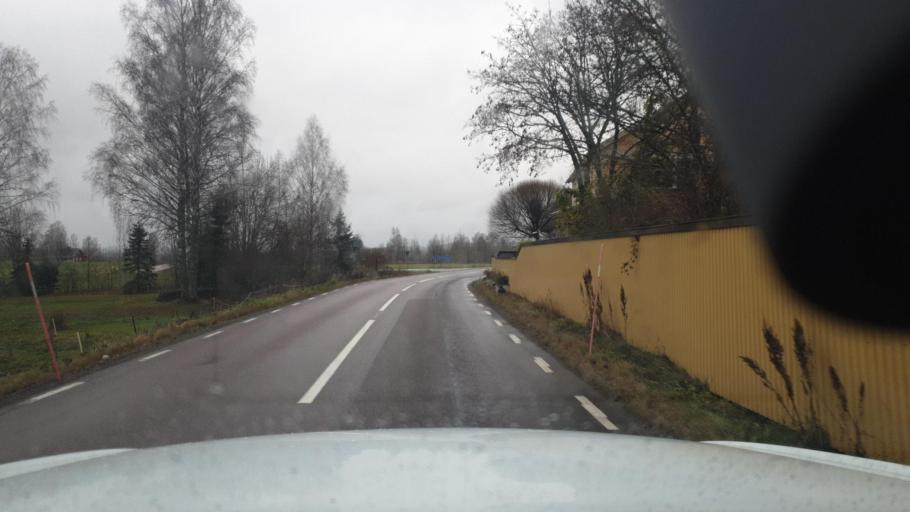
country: SE
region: Vaermland
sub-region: Eda Kommun
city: Amotfors
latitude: 59.7591
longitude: 12.2133
